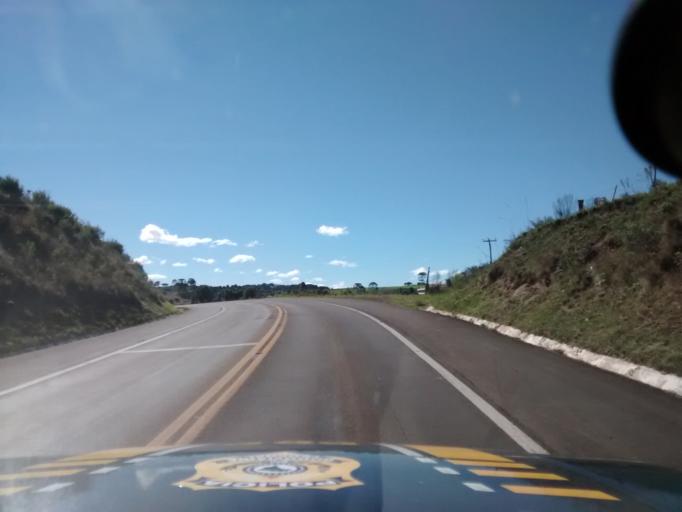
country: BR
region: Rio Grande do Sul
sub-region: Vacaria
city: Vacaria
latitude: -28.3386
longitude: -51.1531
